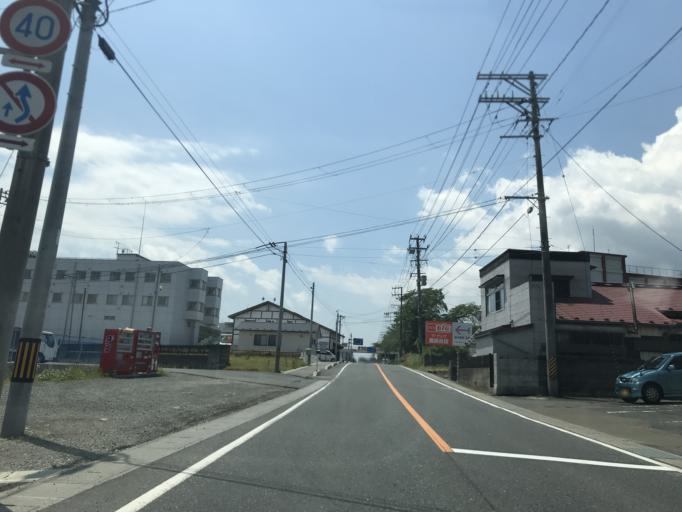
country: JP
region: Miyagi
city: Wakuya
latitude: 38.4803
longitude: 141.0976
